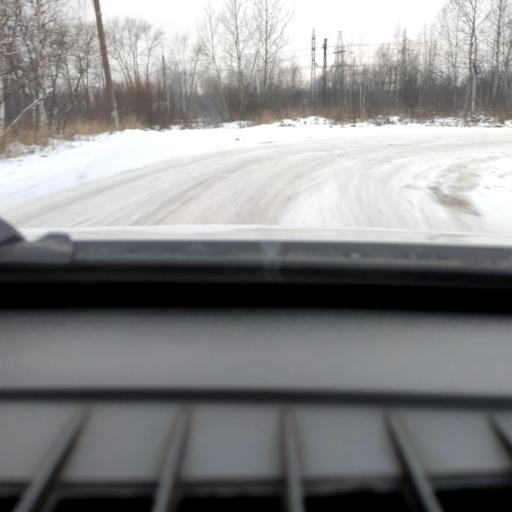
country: RU
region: Perm
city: Perm
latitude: 58.1049
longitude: 56.3631
